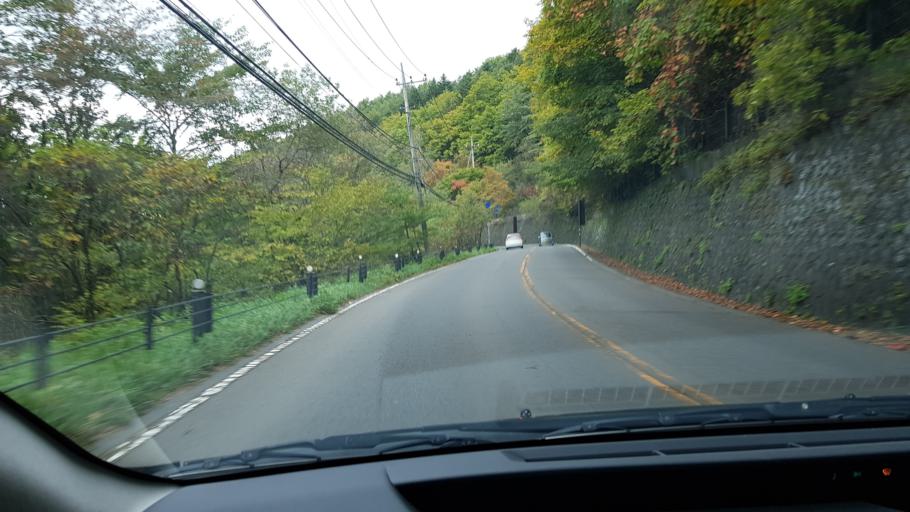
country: JP
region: Nagano
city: Nakano
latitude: 36.6103
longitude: 138.5836
